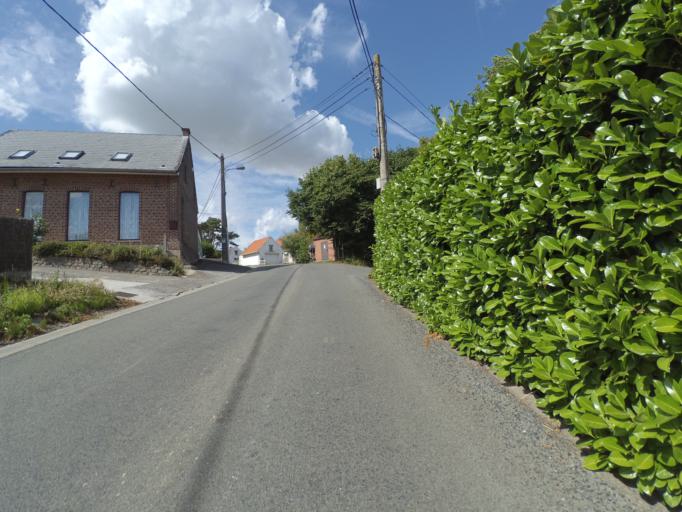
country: BE
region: Wallonia
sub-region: Province du Hainaut
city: Frasnes-lez-Buissenal
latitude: 50.6820
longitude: 3.6068
